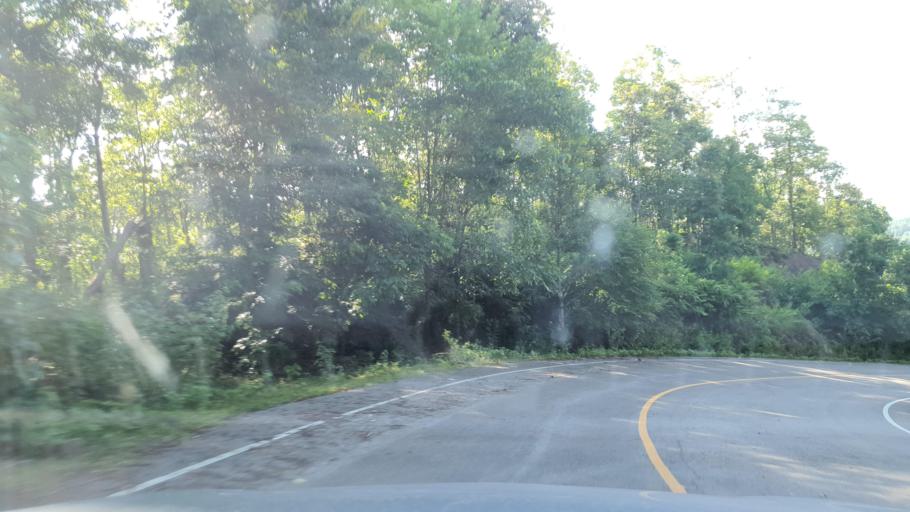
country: TH
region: Chiang Mai
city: Mae On
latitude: 18.7928
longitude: 99.3053
